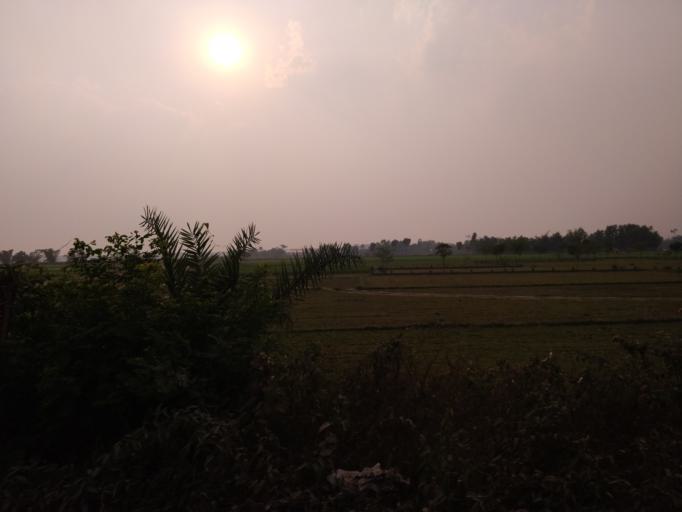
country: BD
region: Sylhet
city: Habiganj
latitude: 24.1404
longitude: 91.3513
